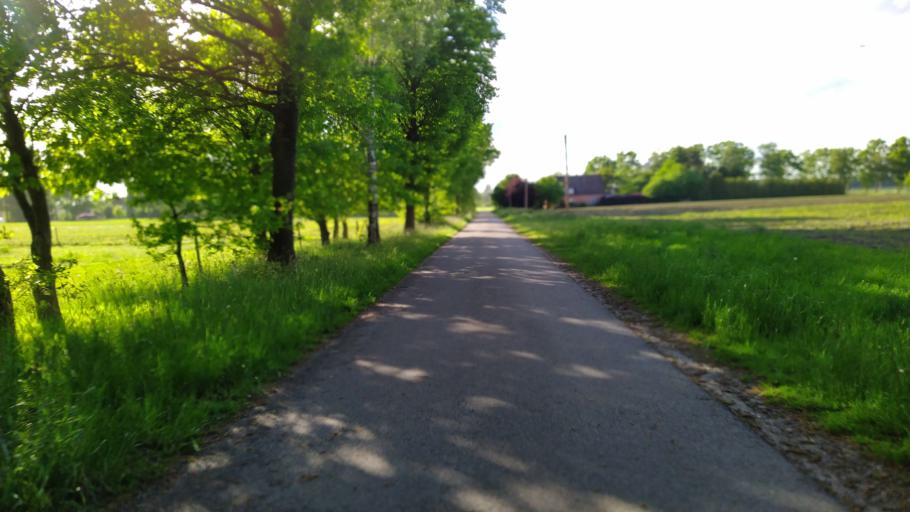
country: DE
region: Lower Saxony
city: Farven
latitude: 53.4499
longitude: 9.2789
